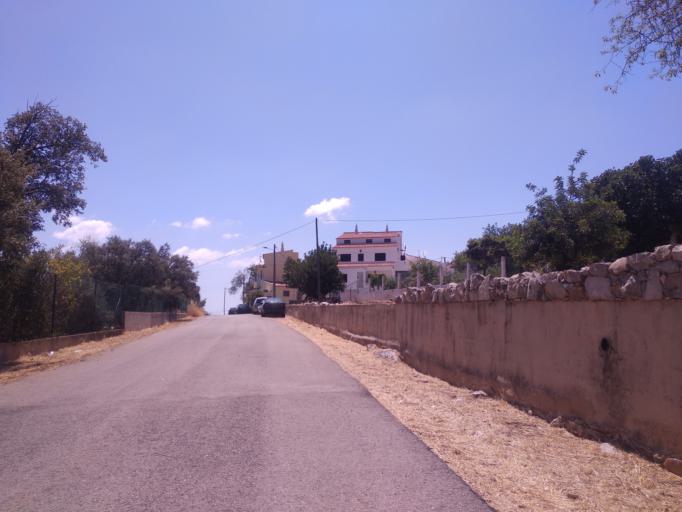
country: PT
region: Faro
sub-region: Sao Bras de Alportel
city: Sao Bras de Alportel
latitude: 37.1618
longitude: -7.9019
